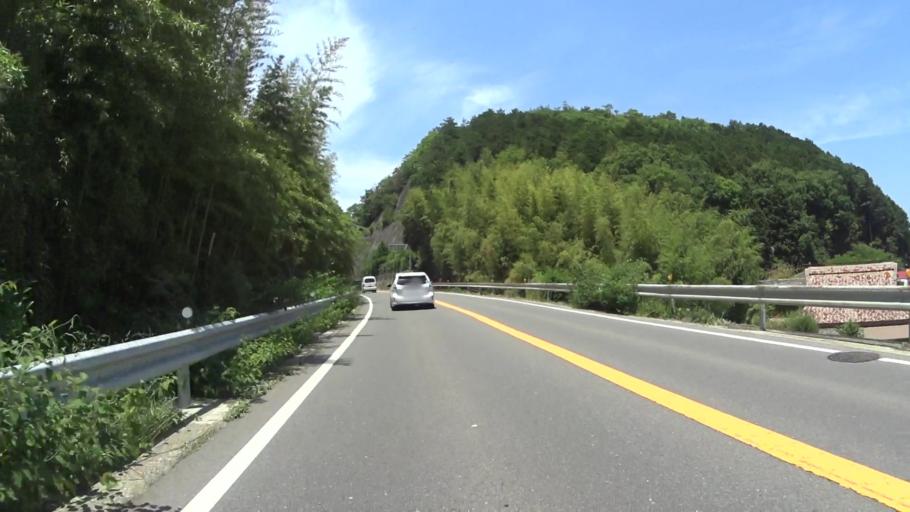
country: JP
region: Kyoto
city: Kameoka
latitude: 35.0805
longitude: 135.5166
